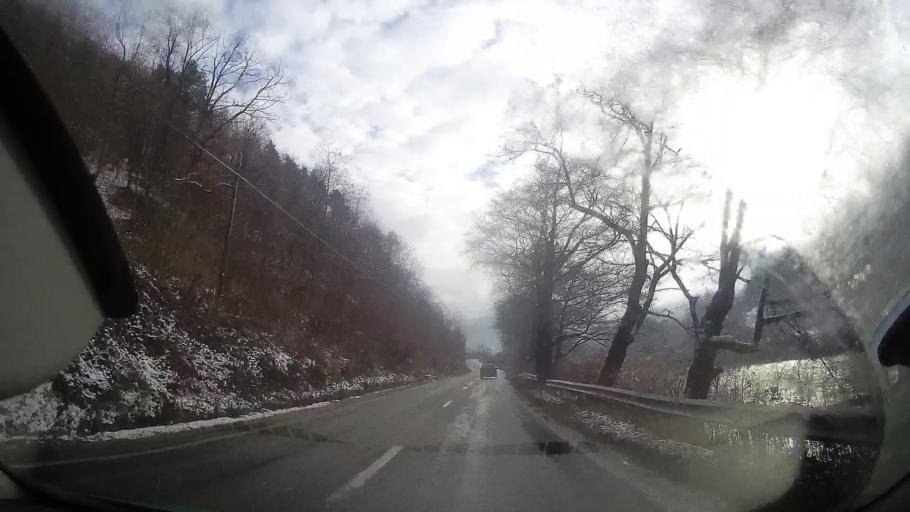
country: RO
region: Alba
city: Salciua de Sus
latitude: 46.3979
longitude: 23.3824
